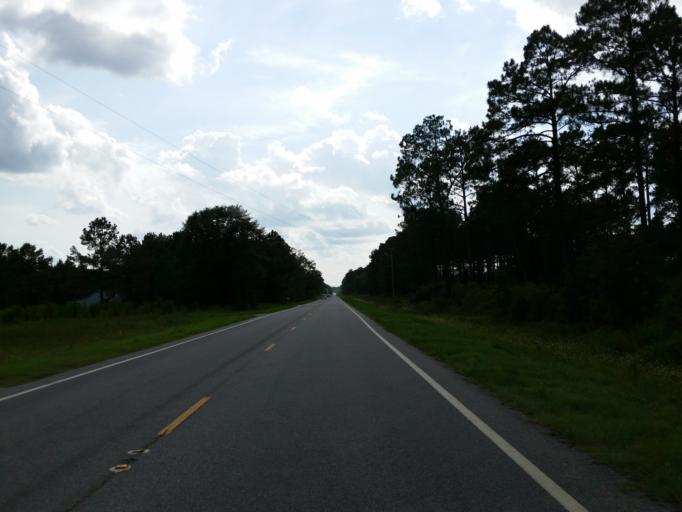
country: US
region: Georgia
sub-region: Lee County
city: Leesburg
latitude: 31.7277
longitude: -83.9735
